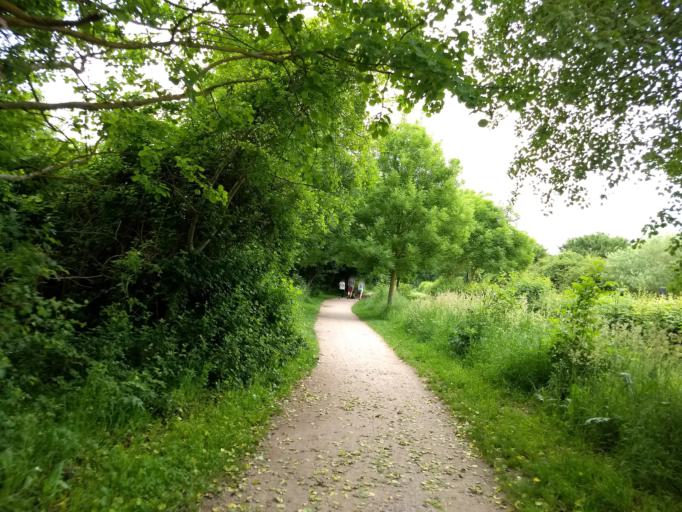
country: GB
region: England
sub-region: Central Bedfordshire
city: Marston Moretaine
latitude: 52.0646
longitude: -0.5380
